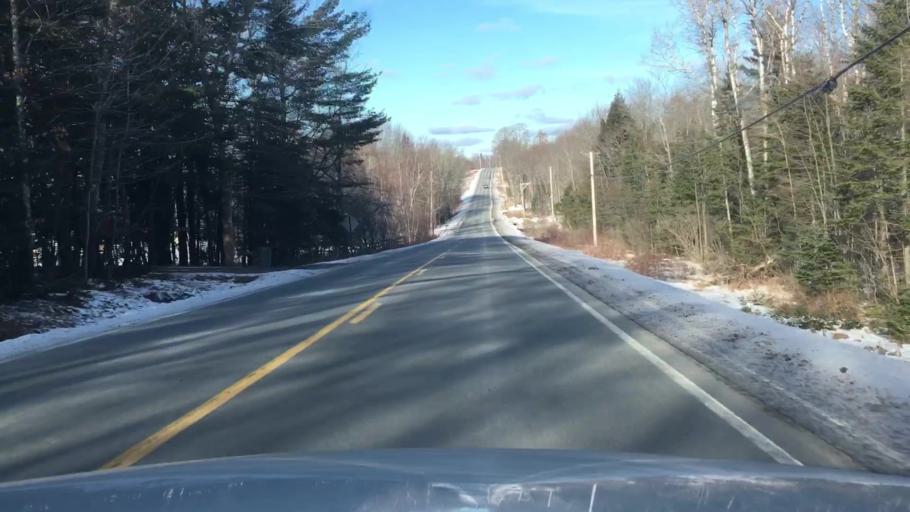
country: US
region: Maine
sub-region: Penobscot County
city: Holden
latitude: 44.7597
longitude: -68.5957
